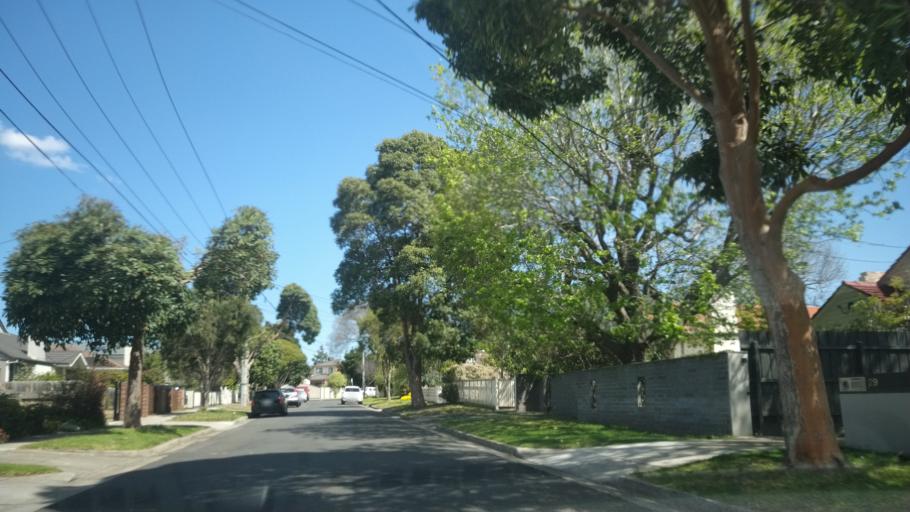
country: AU
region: Victoria
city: Highett
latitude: -37.9465
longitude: 145.0497
